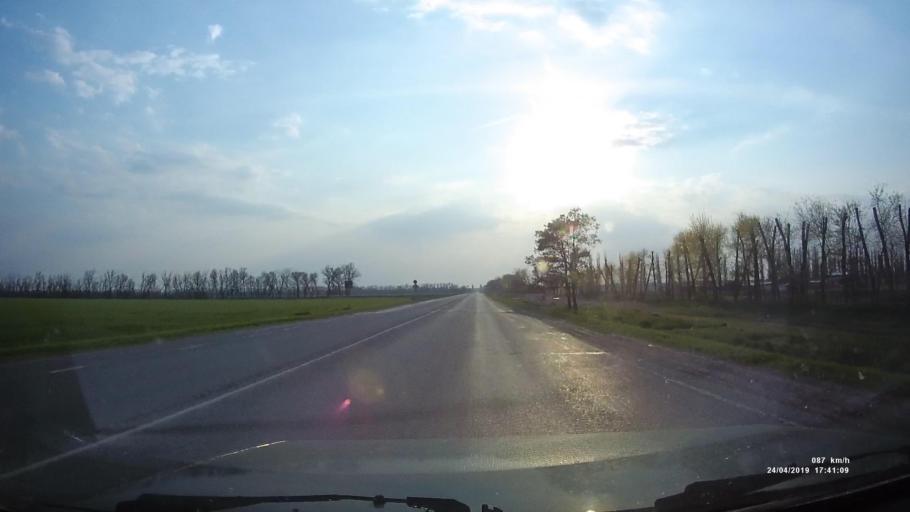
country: RU
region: Rostov
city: Tselina
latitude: 46.5313
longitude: 40.9769
